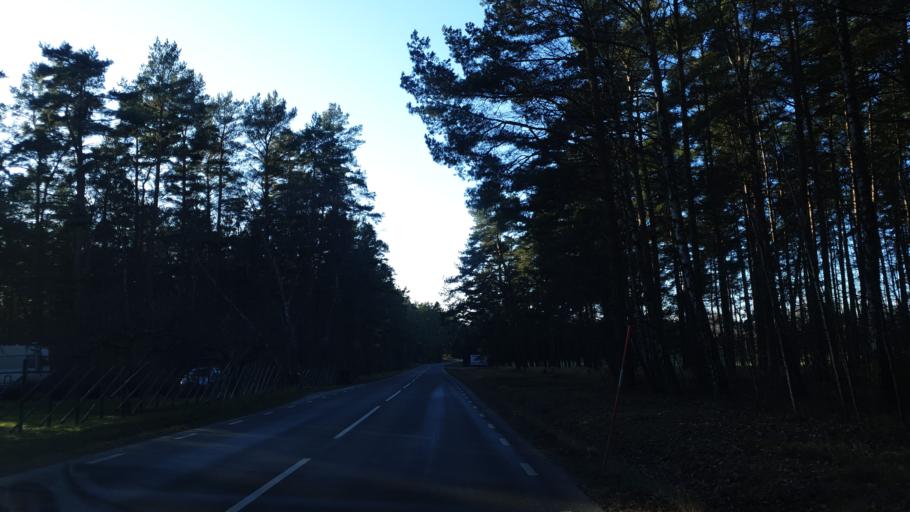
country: SE
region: Blekinge
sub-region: Ronneby Kommun
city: Kallinge
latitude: 56.1974
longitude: 15.3727
